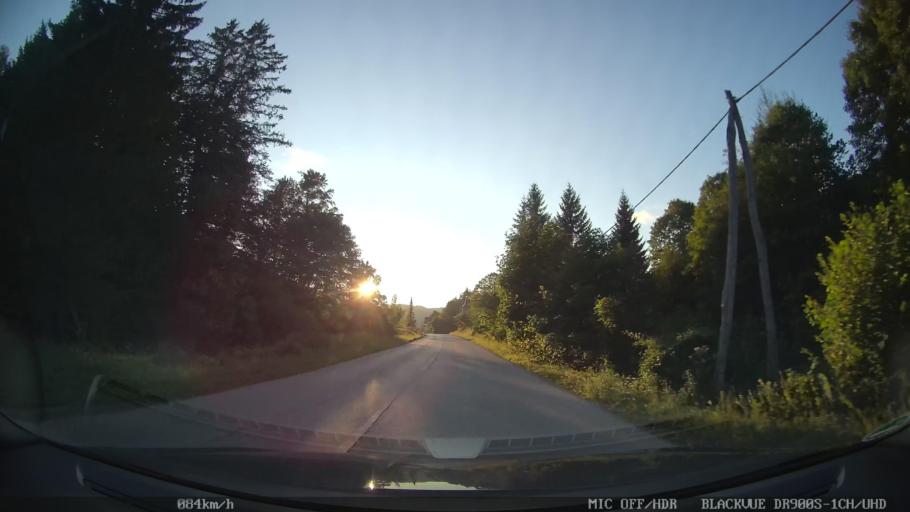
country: HR
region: Karlovacka
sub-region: Grad Ogulin
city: Ogulin
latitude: 45.2411
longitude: 15.1512
